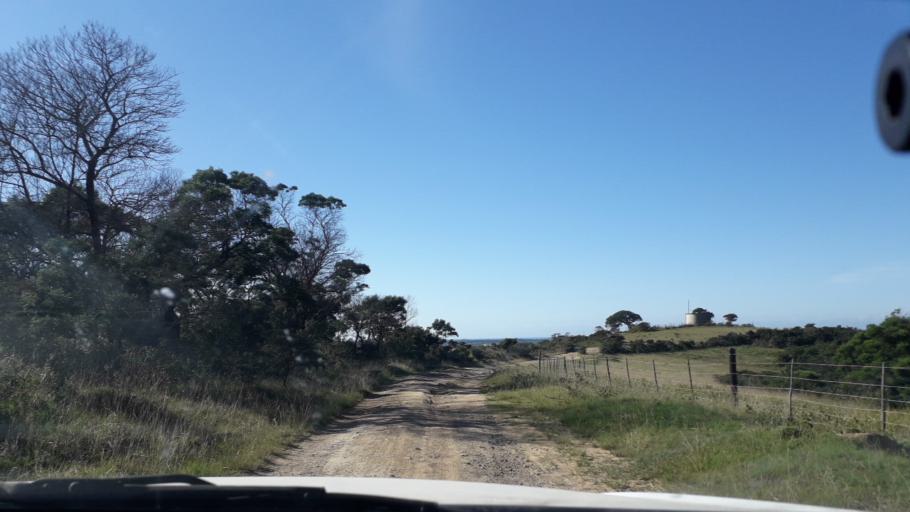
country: ZA
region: Eastern Cape
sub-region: Buffalo City Metropolitan Municipality
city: East London
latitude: -32.8410
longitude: 27.9792
